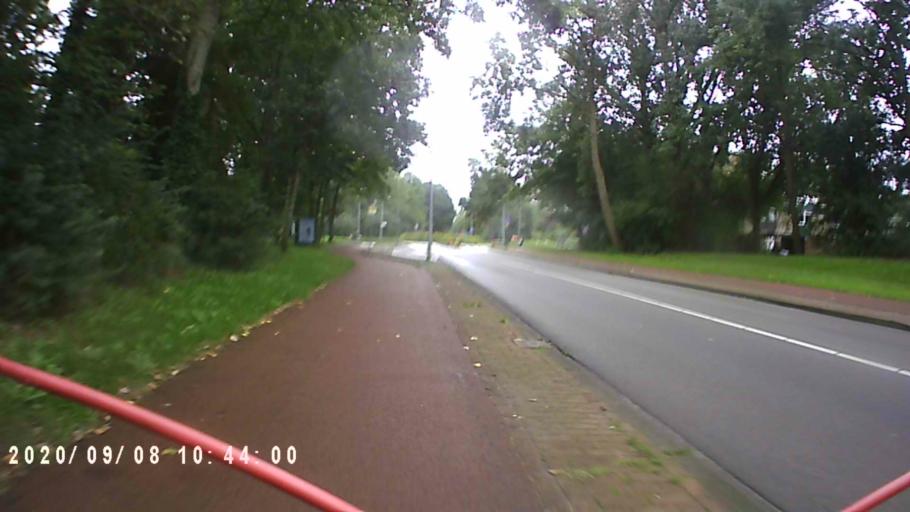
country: NL
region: Groningen
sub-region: Gemeente Groningen
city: Oosterpark
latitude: 53.2356
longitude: 6.6134
